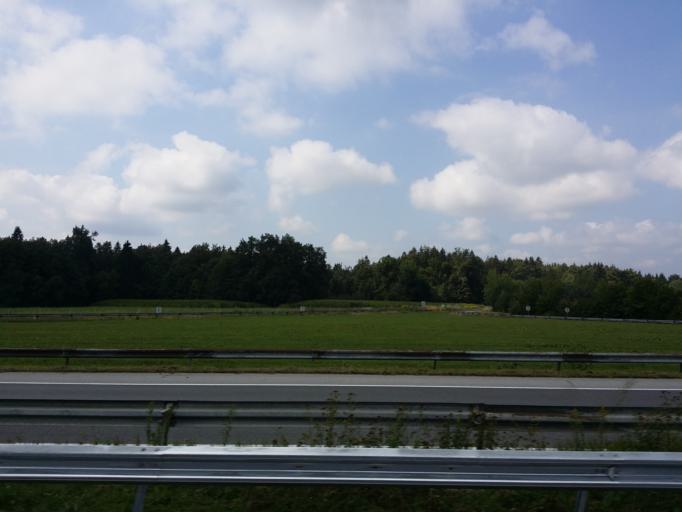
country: SI
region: Sencur
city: Sencur
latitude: 46.2397
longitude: 14.4007
